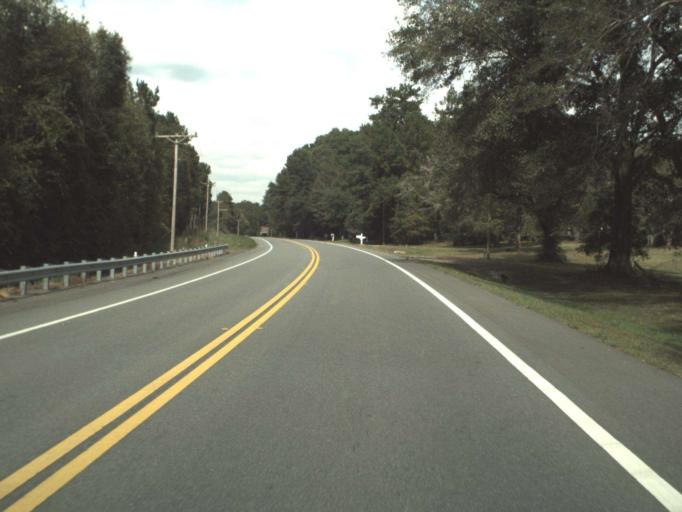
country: US
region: Florida
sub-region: Gadsden County
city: Quincy
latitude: 30.5037
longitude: -84.6085
